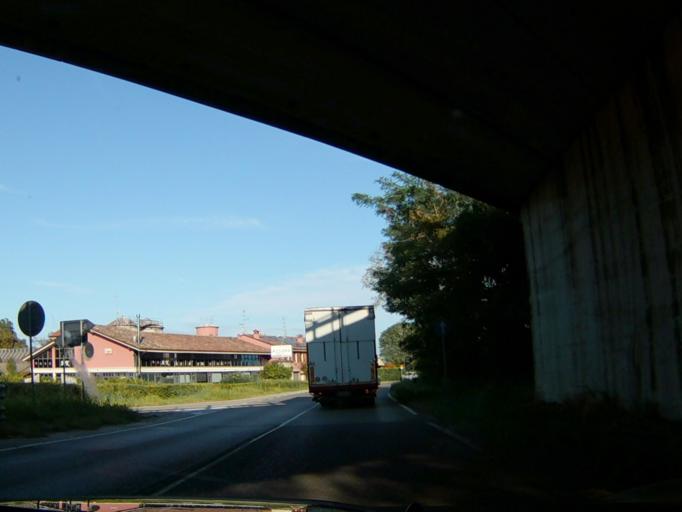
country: IT
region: Lombardy
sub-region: Provincia di Brescia
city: Lonato
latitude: 45.4622
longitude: 10.5076
